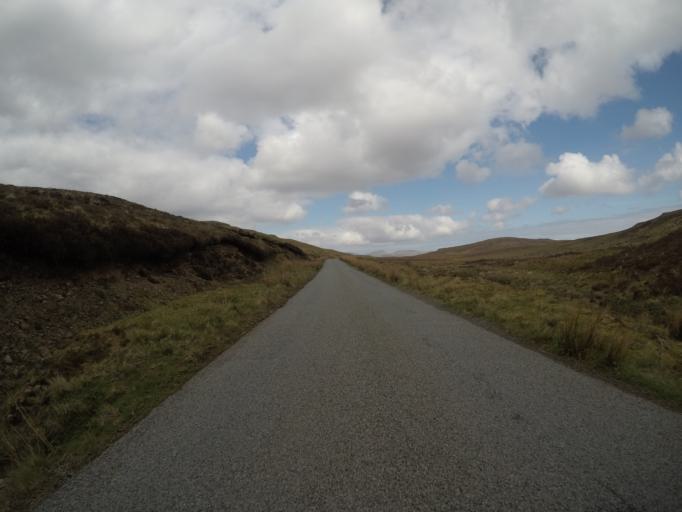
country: GB
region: Scotland
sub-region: Highland
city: Isle of Skye
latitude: 57.3853
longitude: -6.3526
